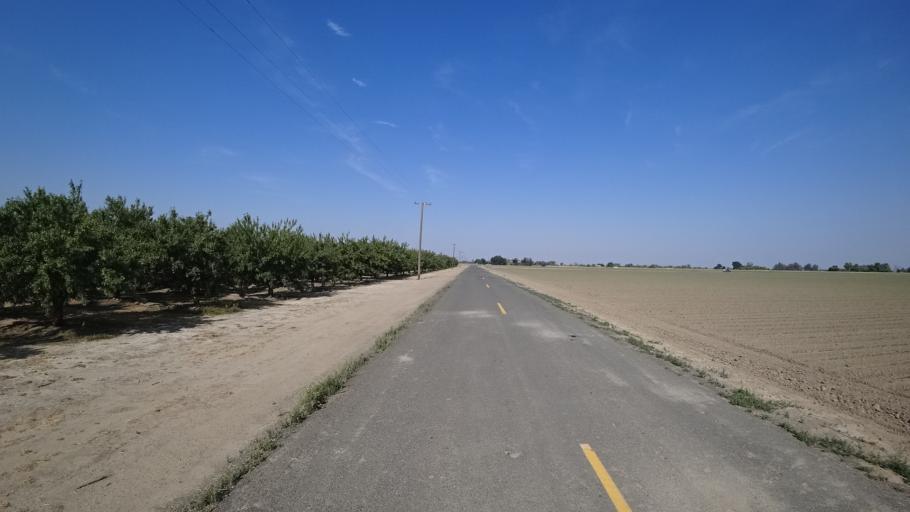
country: US
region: California
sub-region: Kings County
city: Lemoore
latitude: 36.3366
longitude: -119.8574
